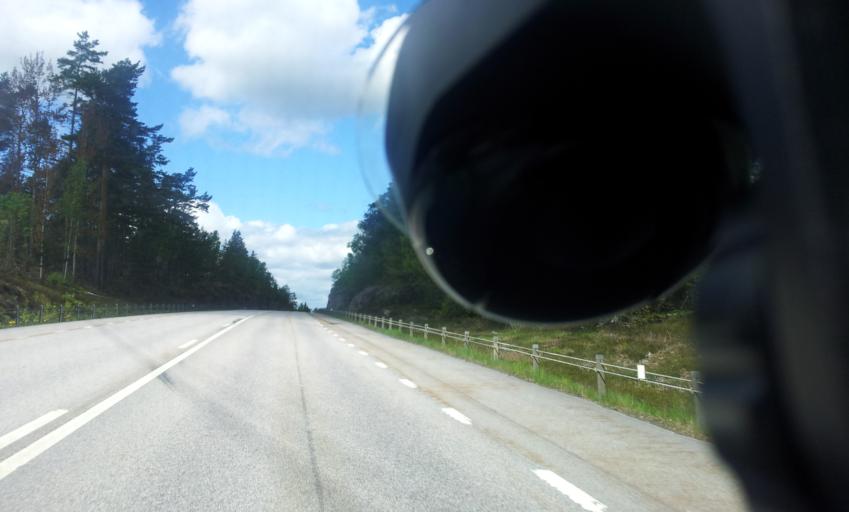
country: SE
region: Kalmar
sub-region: Vasterviks Kommun
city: Ankarsrum
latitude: 57.5347
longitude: 16.4835
